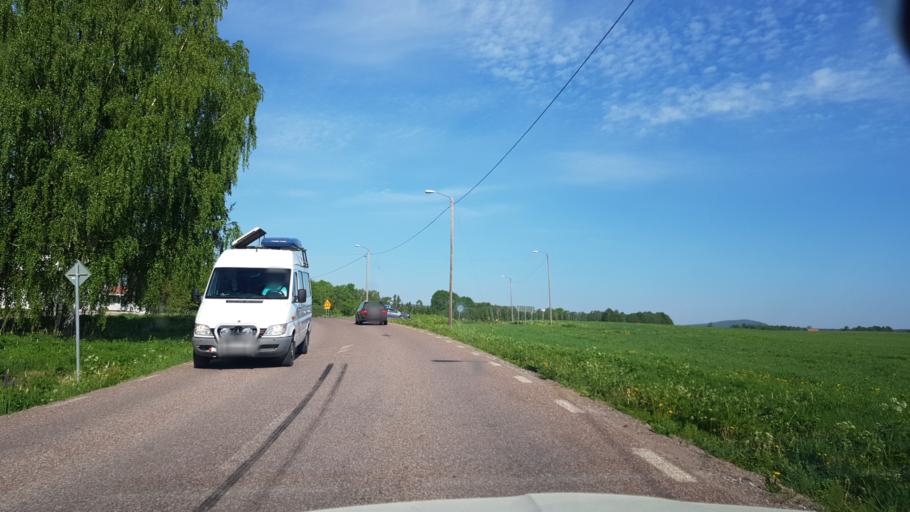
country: SE
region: Dalarna
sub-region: Saters Kommun
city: Saeter
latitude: 60.4157
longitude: 15.7855
